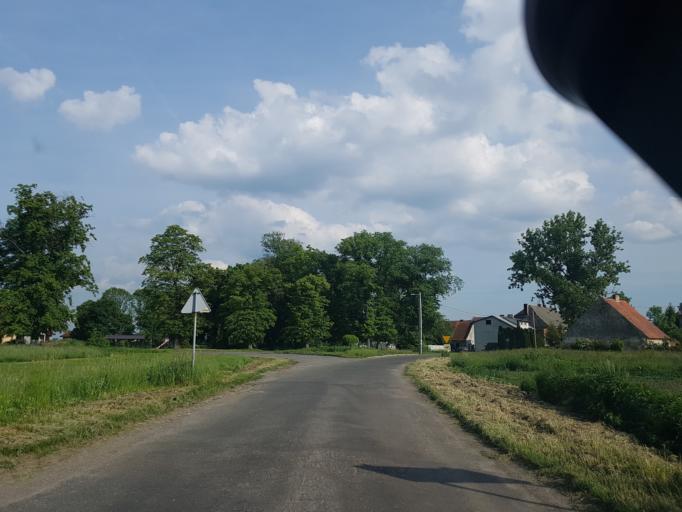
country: PL
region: Lower Silesian Voivodeship
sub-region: Powiat olawski
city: Wierzbno
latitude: 50.8699
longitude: 17.1558
